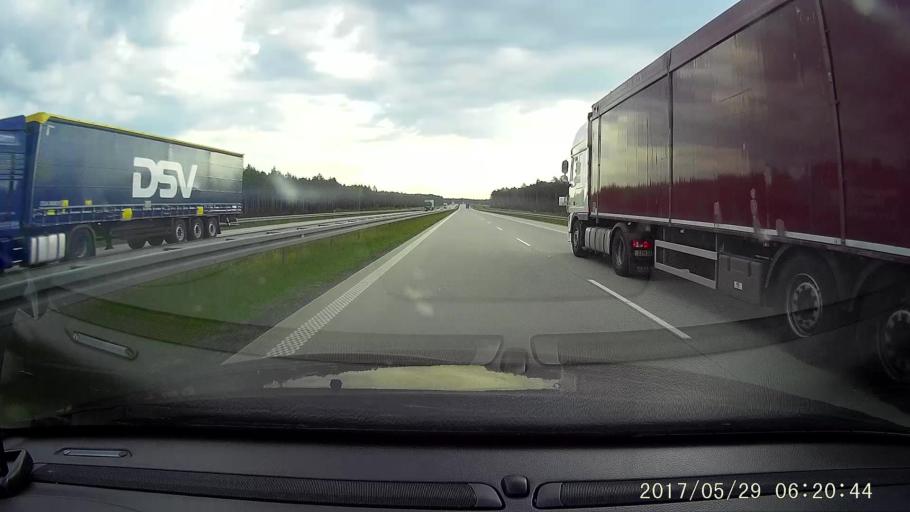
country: PL
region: Lower Silesian Voivodeship
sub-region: Powiat boleslawiecki
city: Boleslawiec
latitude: 51.2956
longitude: 15.4985
